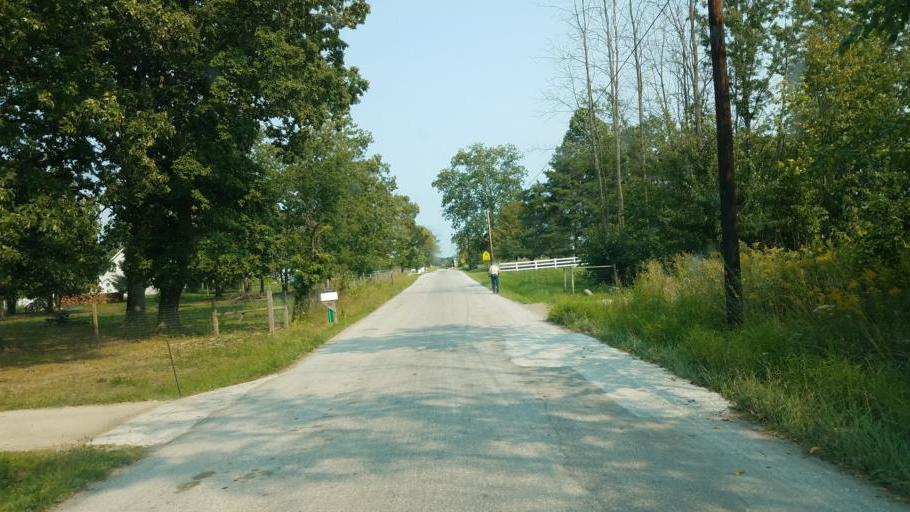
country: US
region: Ohio
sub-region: Geauga County
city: Middlefield
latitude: 41.4939
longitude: -81.0078
